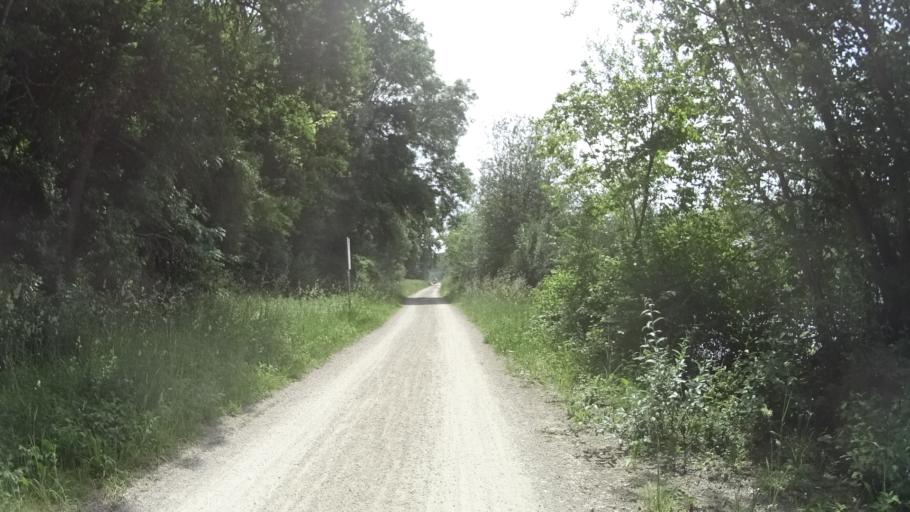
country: DE
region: Bavaria
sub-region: Lower Bavaria
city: Saal
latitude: 48.9095
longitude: 11.9394
